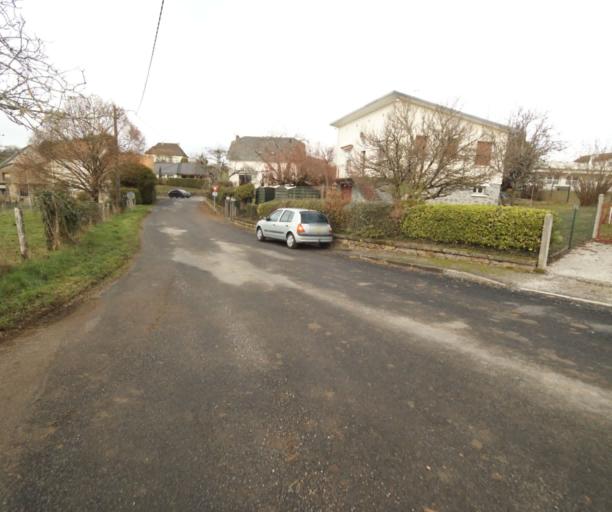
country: FR
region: Limousin
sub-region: Departement de la Correze
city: Chameyrat
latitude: 45.2645
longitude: 1.7222
